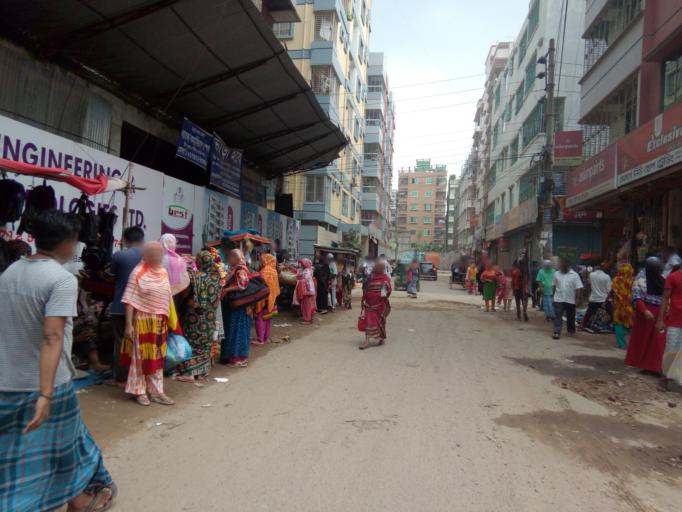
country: BD
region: Dhaka
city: Paltan
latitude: 23.7611
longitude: 90.4426
